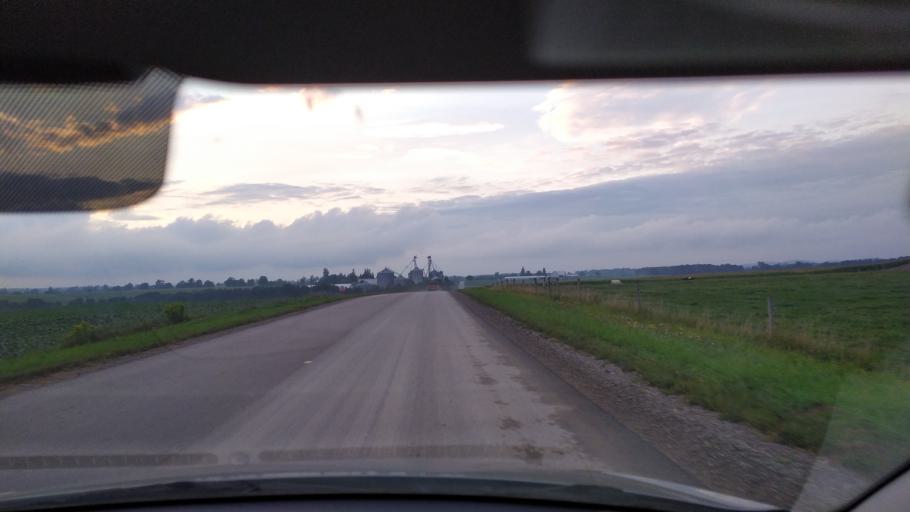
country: CA
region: Ontario
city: Kitchener
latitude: 43.3294
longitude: -80.6199
